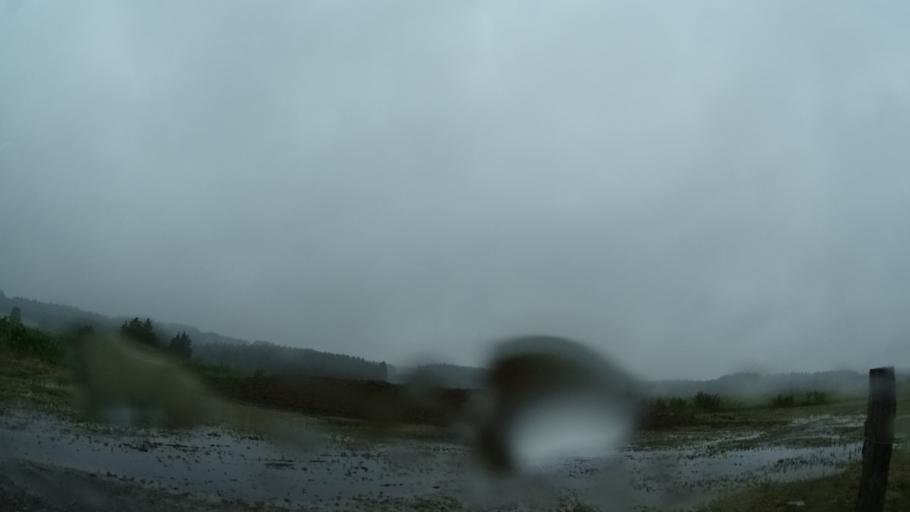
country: BE
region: Wallonia
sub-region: Province de Namur
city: Bievre
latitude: 49.9532
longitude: 5.0227
